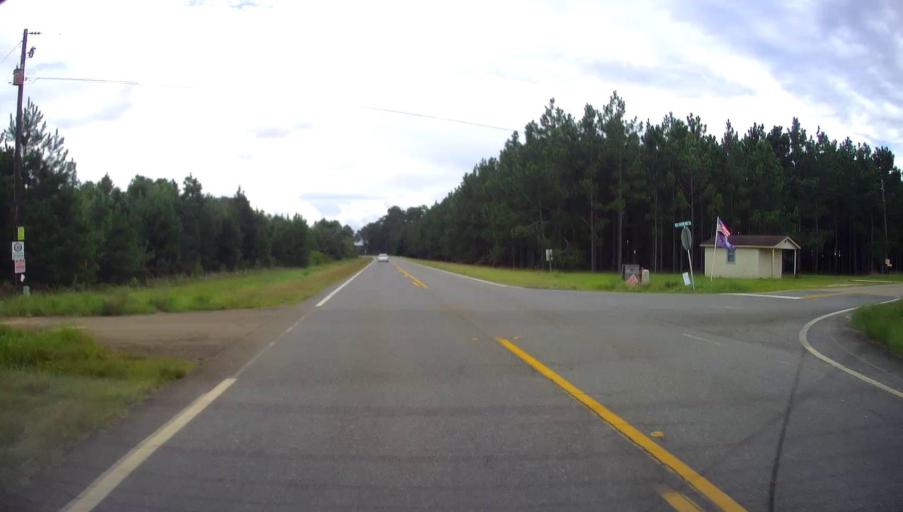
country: US
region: Georgia
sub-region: Marion County
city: Buena Vista
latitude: 32.2688
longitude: -84.4313
